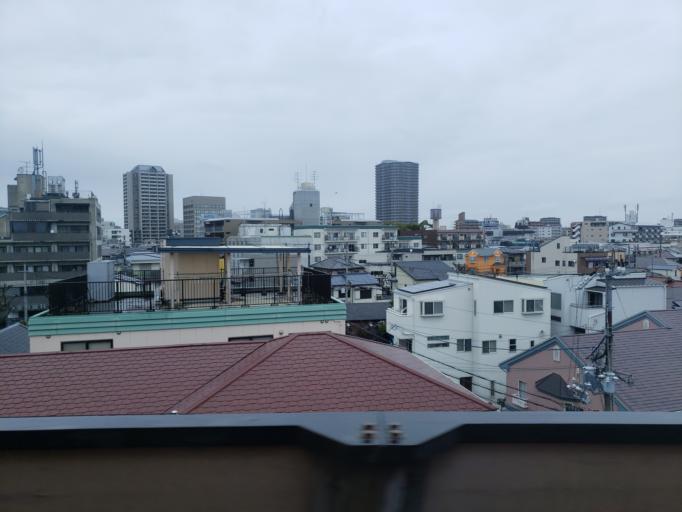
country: JP
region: Hyogo
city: Nishinomiya-hama
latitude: 34.7342
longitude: 135.3475
